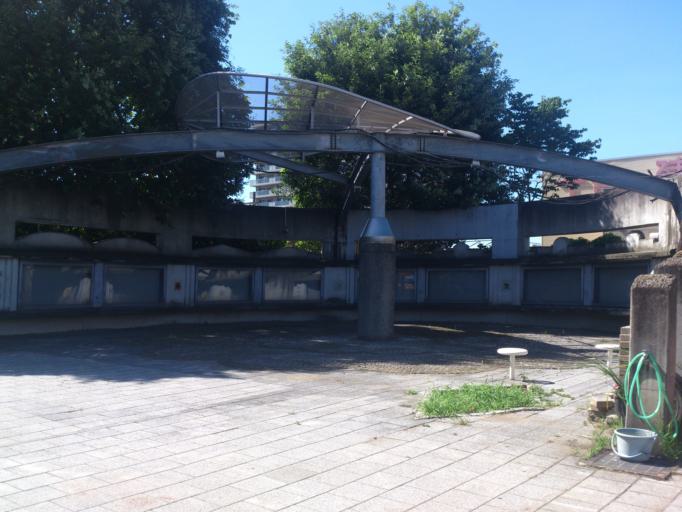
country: JP
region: Ibaraki
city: Ushiku
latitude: 35.9758
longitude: 140.1416
